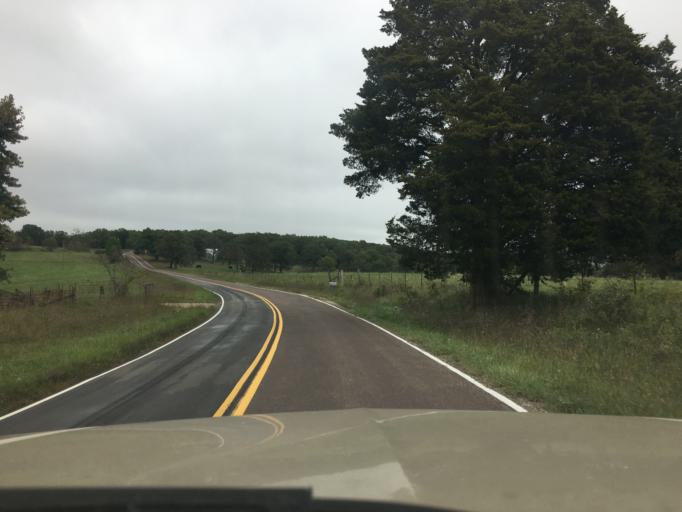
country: US
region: Missouri
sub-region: Crawford County
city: Cuba
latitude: 38.1910
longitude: -91.4703
